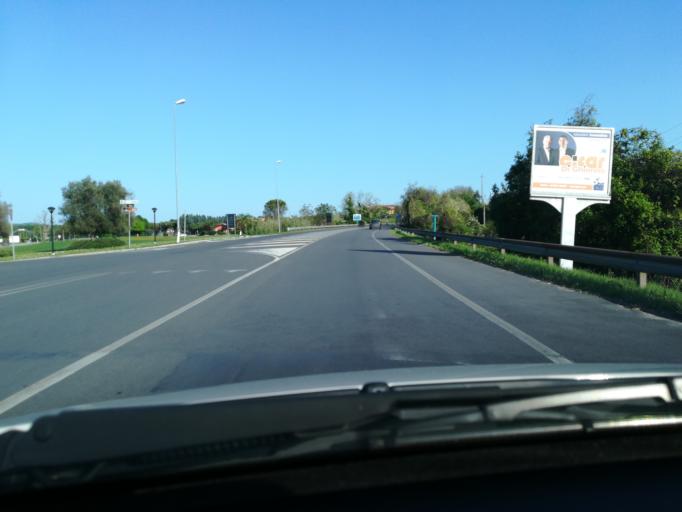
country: IT
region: Emilia-Romagna
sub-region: Provincia di Rimini
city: Misano Adriatico
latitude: 43.9686
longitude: 12.7076
